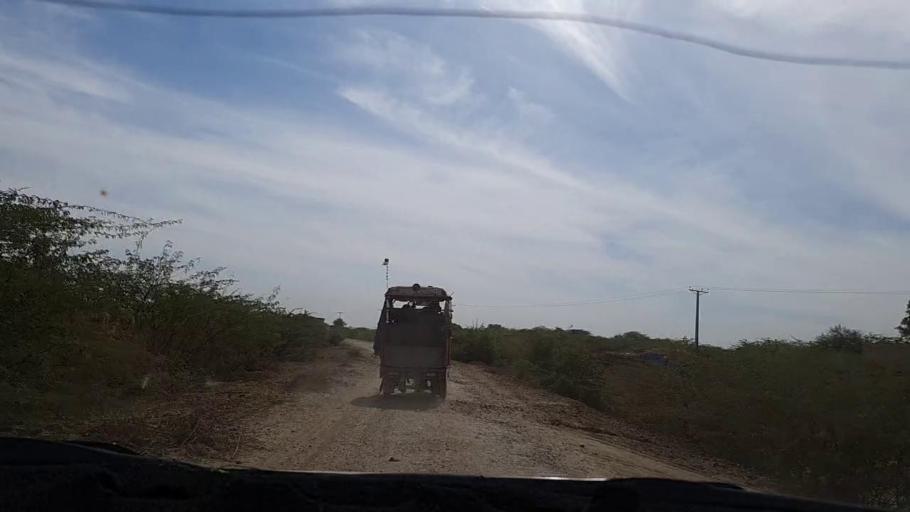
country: PK
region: Sindh
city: Pithoro
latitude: 25.4642
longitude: 69.4554
